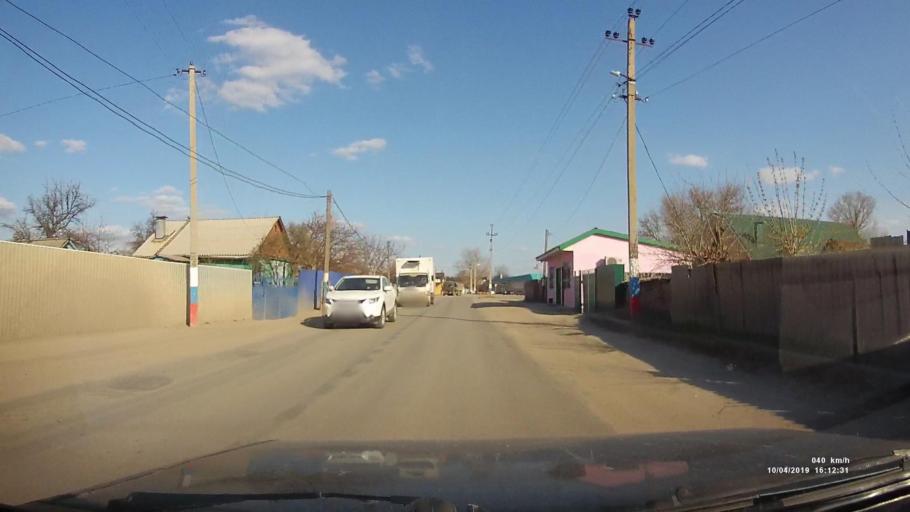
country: RU
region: Rostov
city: Staraya Stanitsa
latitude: 48.3480
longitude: 40.2853
